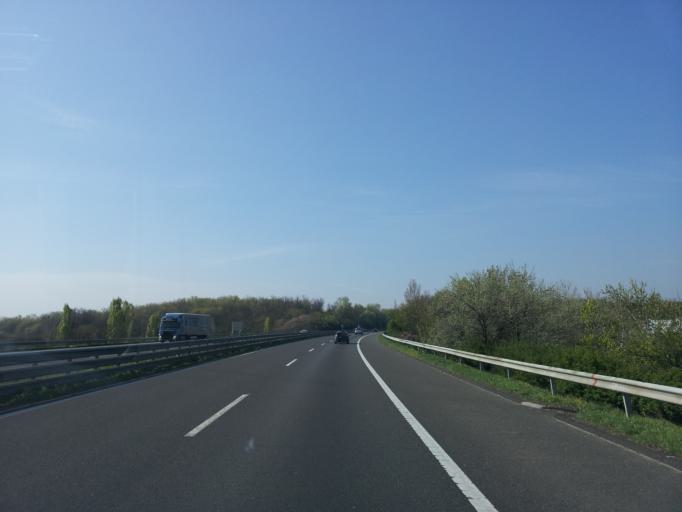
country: HU
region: Fejer
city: Baracska
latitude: 47.3004
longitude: 18.7403
